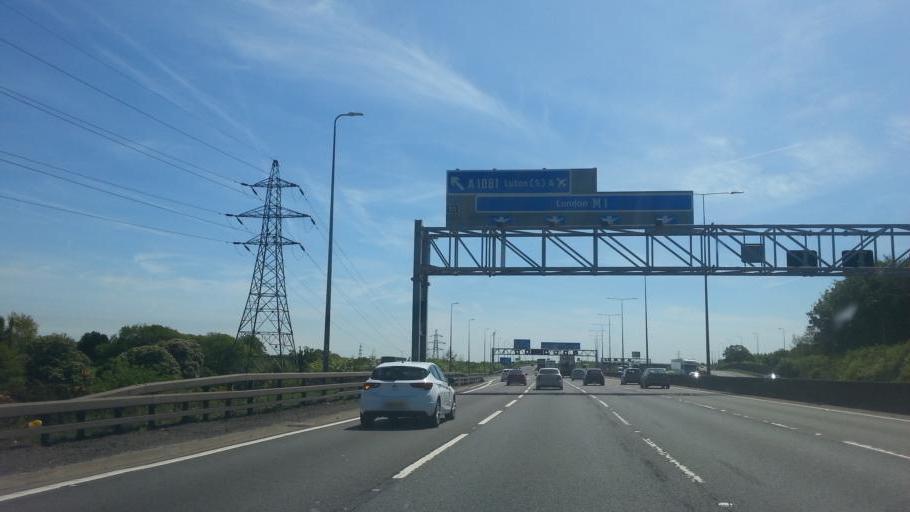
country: GB
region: England
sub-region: Luton
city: Luton
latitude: 51.8597
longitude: -0.4296
